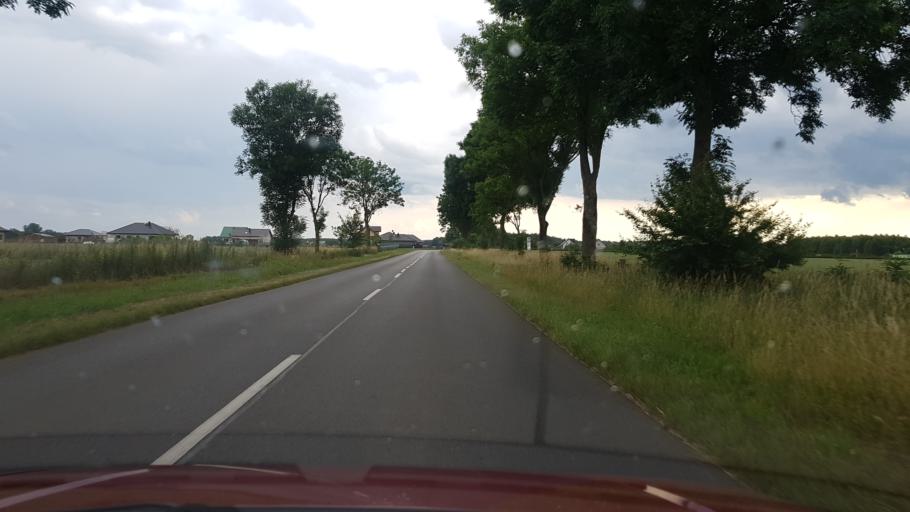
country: PL
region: West Pomeranian Voivodeship
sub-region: Powiat gryficki
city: Gryfice
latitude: 53.8950
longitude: 15.1767
